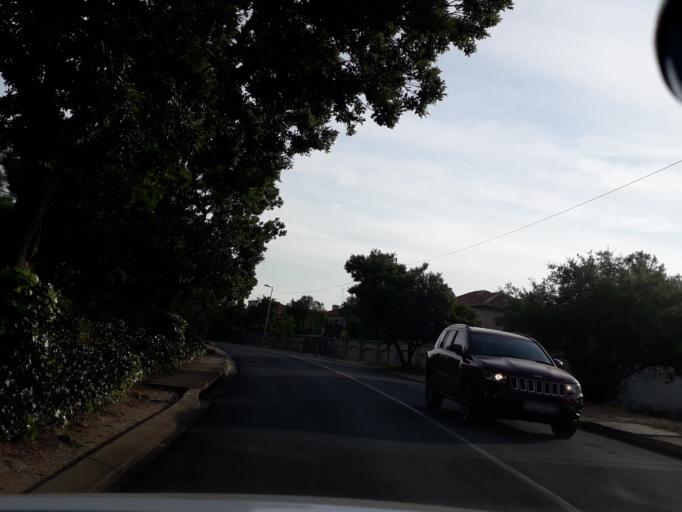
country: ZA
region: Gauteng
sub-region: City of Johannesburg Metropolitan Municipality
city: Diepsloot
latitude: -26.0676
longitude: 27.9874
